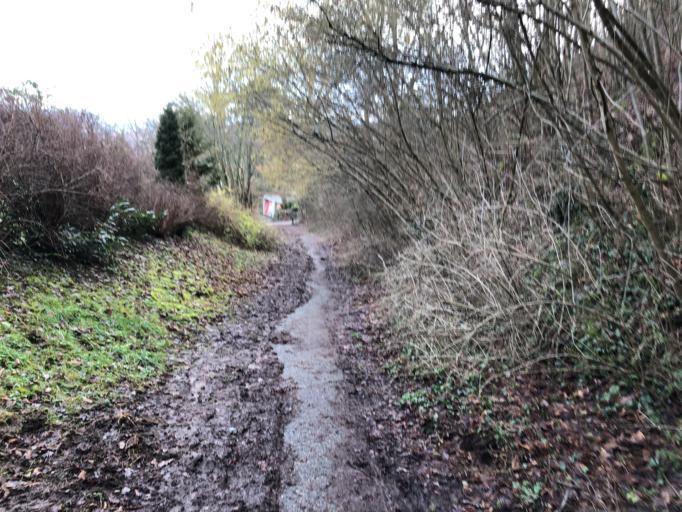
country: DE
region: Baden-Wuerttemberg
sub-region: Tuebingen Region
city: Tuebingen
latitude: 48.5266
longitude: 9.0358
